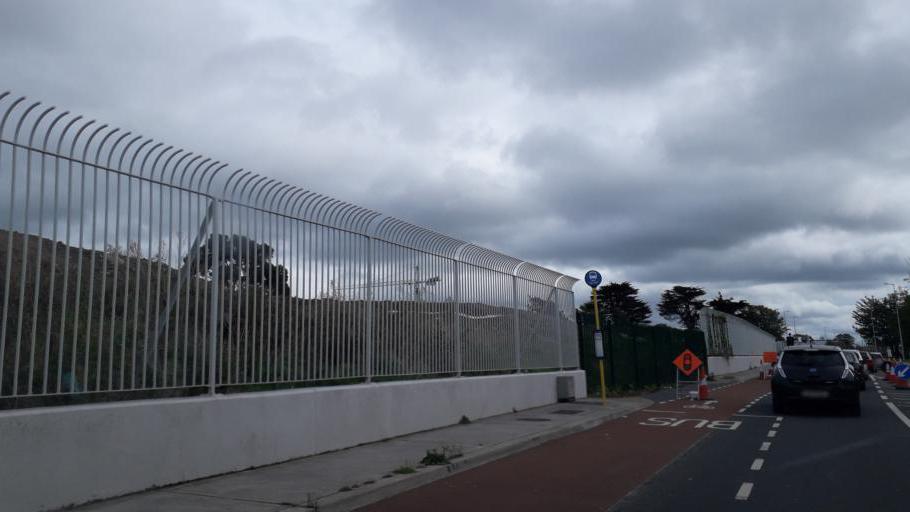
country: IE
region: Leinster
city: Cabinteely
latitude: 53.2761
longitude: -6.1559
